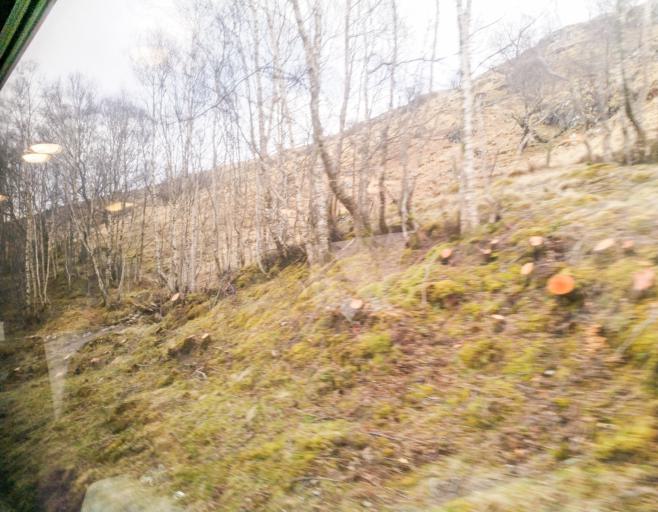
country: GB
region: Scotland
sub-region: Highland
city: Spean Bridge
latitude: 56.7965
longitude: -4.7231
